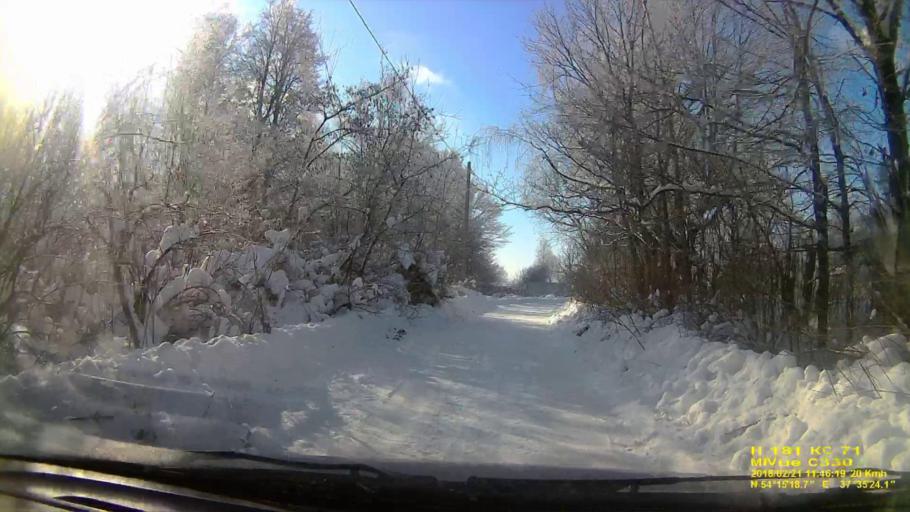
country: RU
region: Tula
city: Gorelki
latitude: 54.2552
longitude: 37.5899
